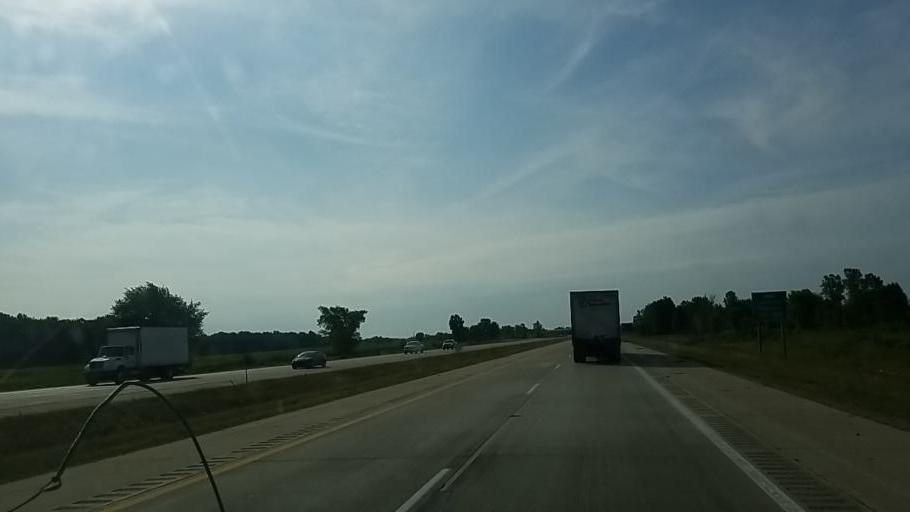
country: US
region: Michigan
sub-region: Clinton County
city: Wacousta
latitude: 42.7941
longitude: -84.6836
